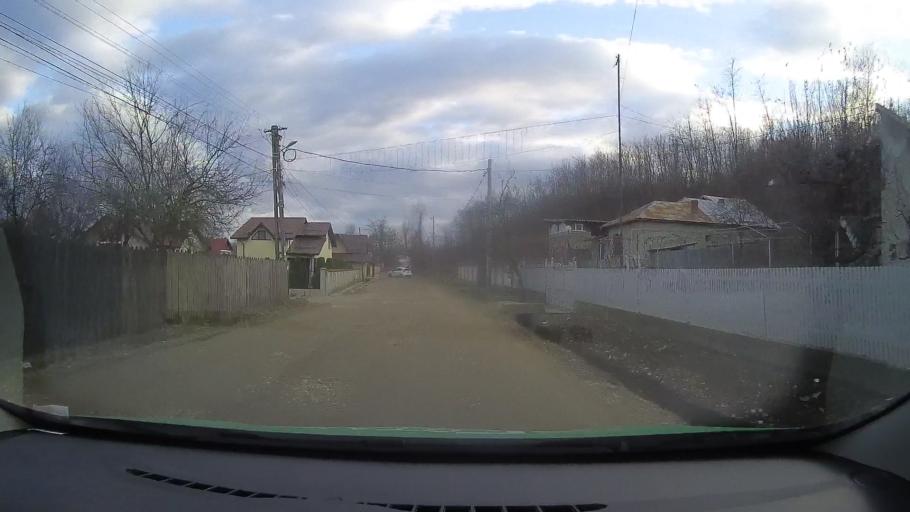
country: RO
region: Dambovita
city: Ion Luca Caragiale
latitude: 44.9117
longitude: 25.6935
